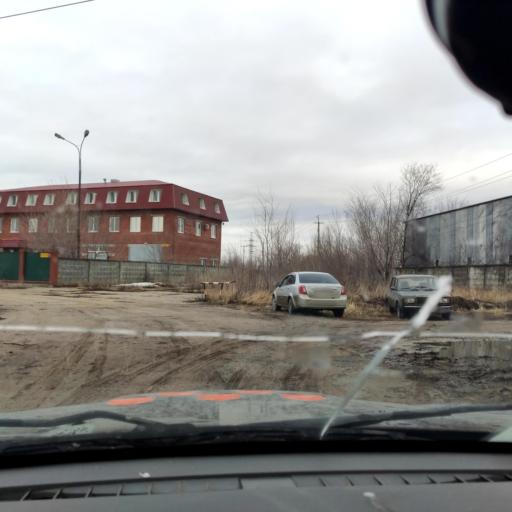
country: RU
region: Samara
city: Tol'yatti
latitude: 53.5616
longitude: 49.3404
